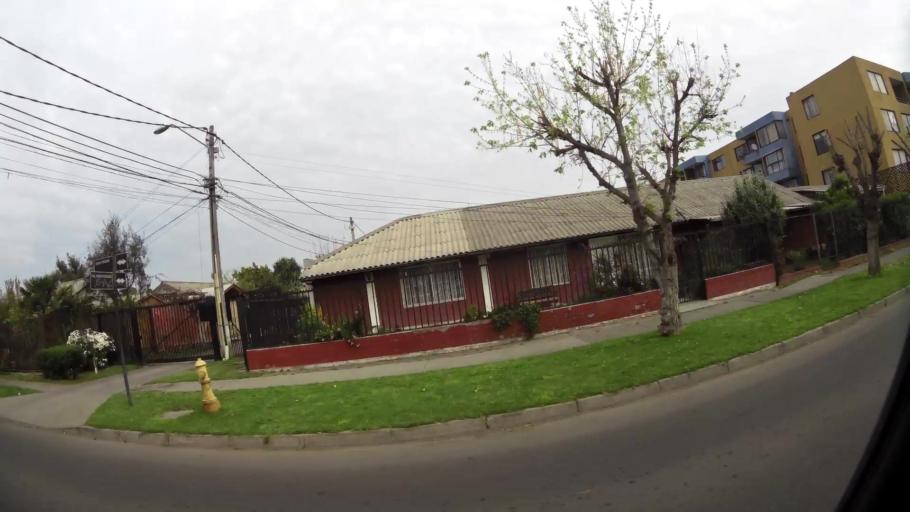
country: CL
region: Santiago Metropolitan
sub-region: Provincia de Santiago
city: Lo Prado
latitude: -33.5241
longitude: -70.7600
